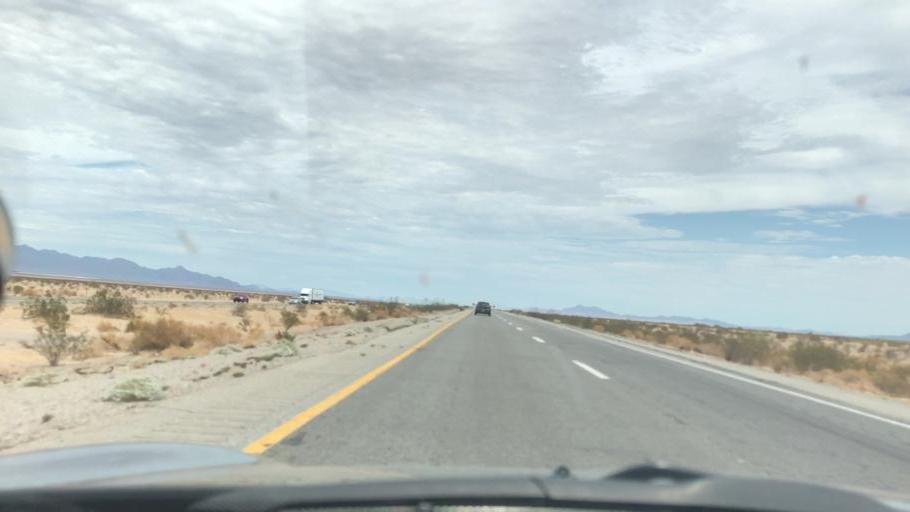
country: US
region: California
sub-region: Riverside County
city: Mesa Verde
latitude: 33.6401
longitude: -115.0986
